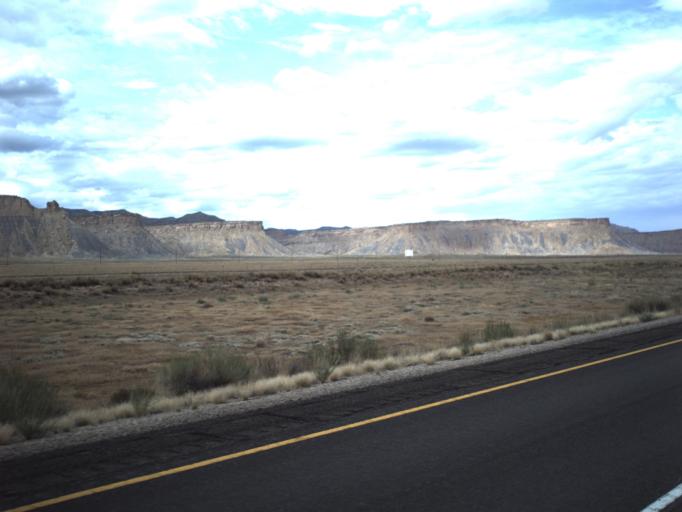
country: US
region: Utah
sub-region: Grand County
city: Moab
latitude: 38.9484
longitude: -109.7823
